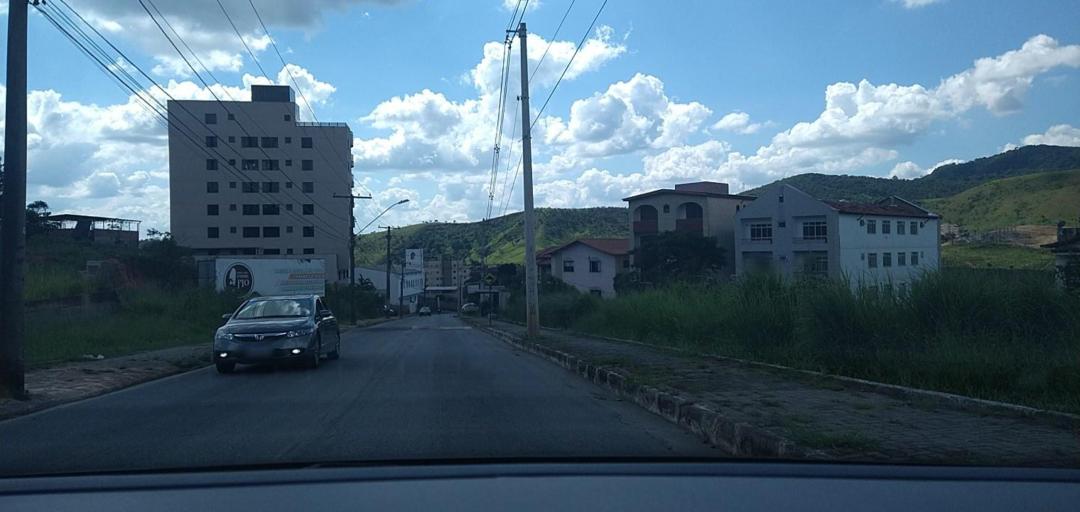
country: BR
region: Minas Gerais
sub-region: Joao Monlevade
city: Joao Monlevade
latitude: -19.8157
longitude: -43.1908
